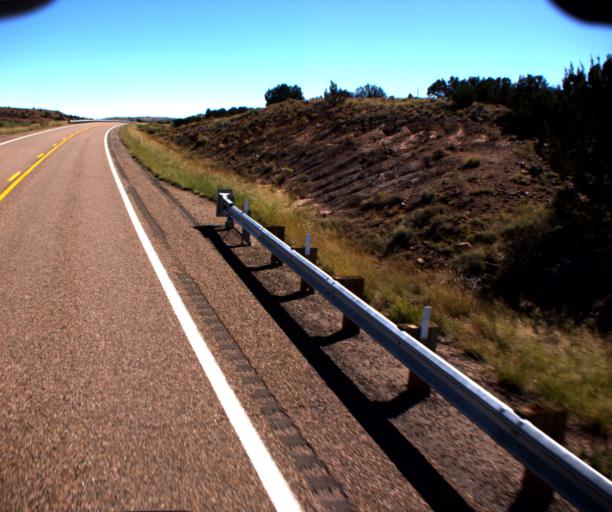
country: US
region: Arizona
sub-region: Apache County
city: Saint Johns
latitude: 34.5876
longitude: -109.5518
